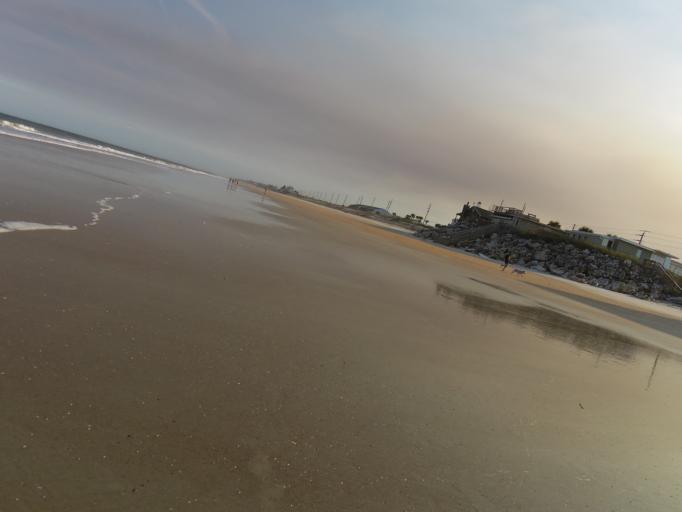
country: US
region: Florida
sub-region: Saint Johns County
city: Villano Beach
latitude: 29.9368
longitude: -81.2984
